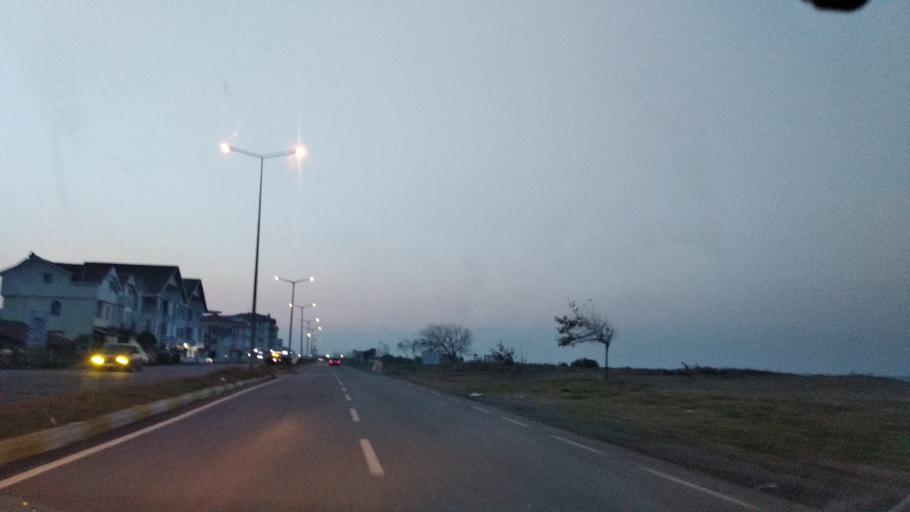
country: TR
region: Sakarya
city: Karasu
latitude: 41.0961
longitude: 30.7309
